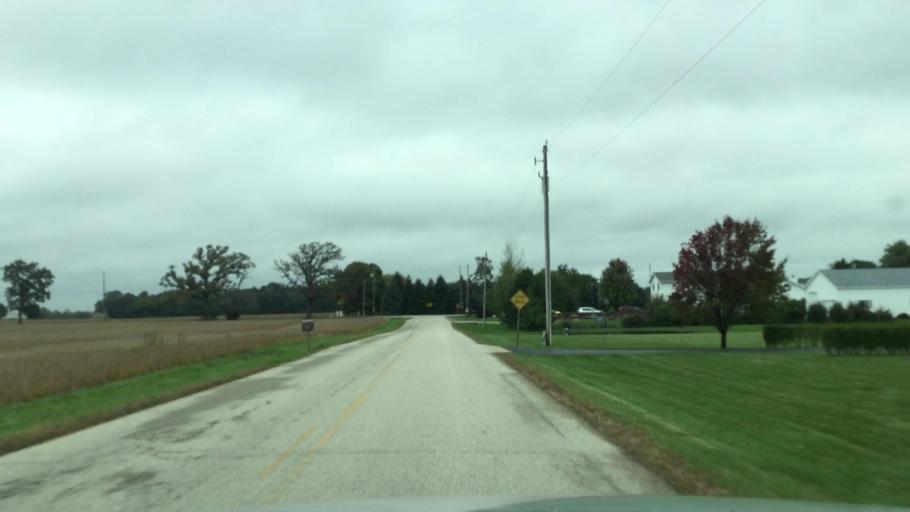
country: US
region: Wisconsin
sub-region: Racine County
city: Eagle Lake
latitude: 42.7549
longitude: -88.1554
